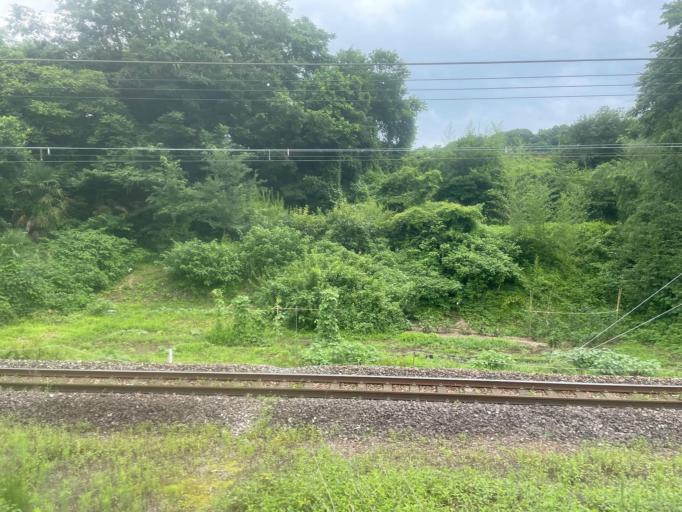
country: JP
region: Gunma
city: Numata
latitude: 36.5628
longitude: 139.0419
